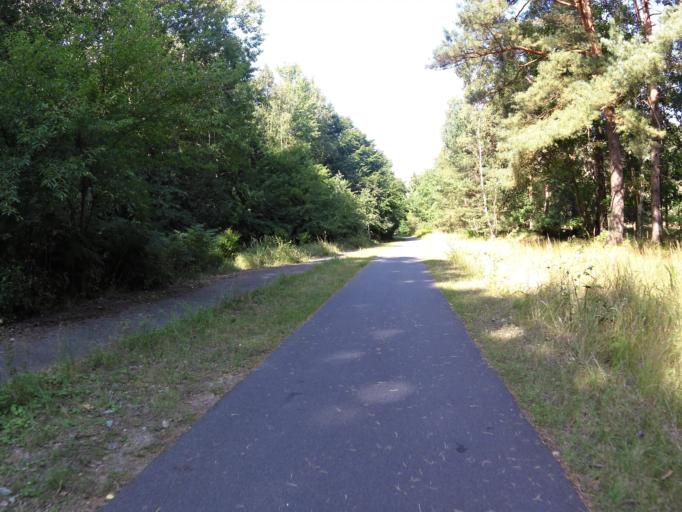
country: DE
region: Mecklenburg-Vorpommern
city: Karlshagen
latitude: 54.1388
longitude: 13.8145
